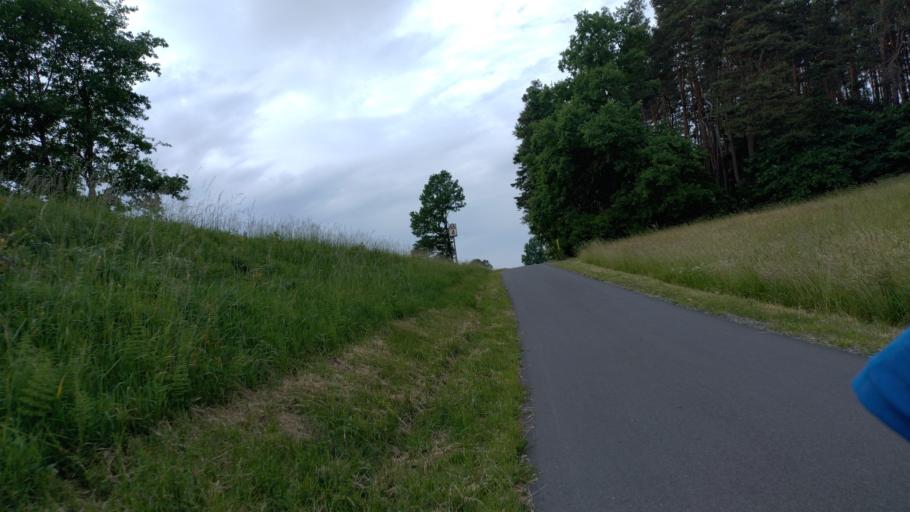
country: DE
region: Bavaria
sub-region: Upper Franconia
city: Harsdorf
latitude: 50.0126
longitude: 11.5841
